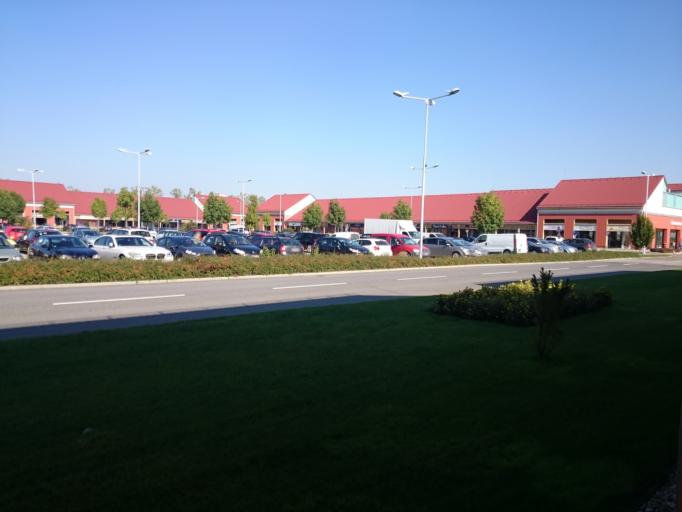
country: HU
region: Hajdu-Bihar
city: Polgar
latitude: 47.8431
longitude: 21.1428
